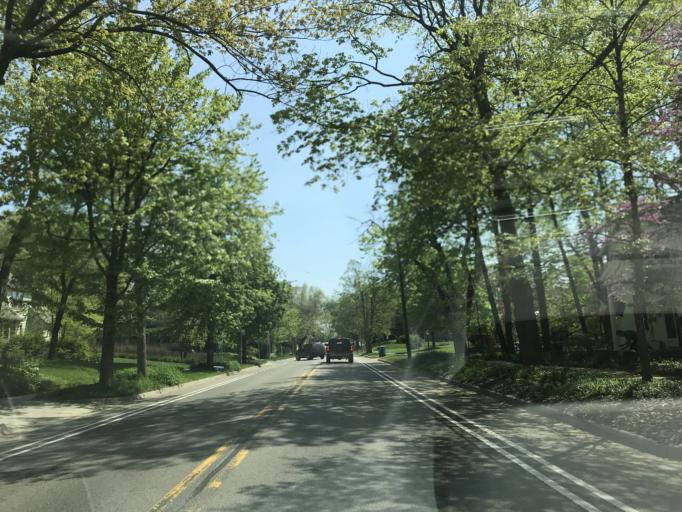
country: US
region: Michigan
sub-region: Washtenaw County
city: Ann Arbor
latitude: 42.2710
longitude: -83.7583
